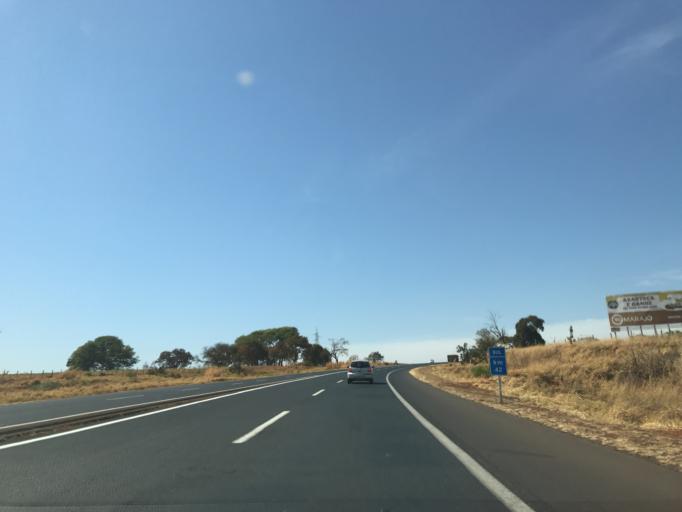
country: BR
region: Minas Gerais
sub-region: Centralina
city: Centralina
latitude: -18.7535
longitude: -49.0800
